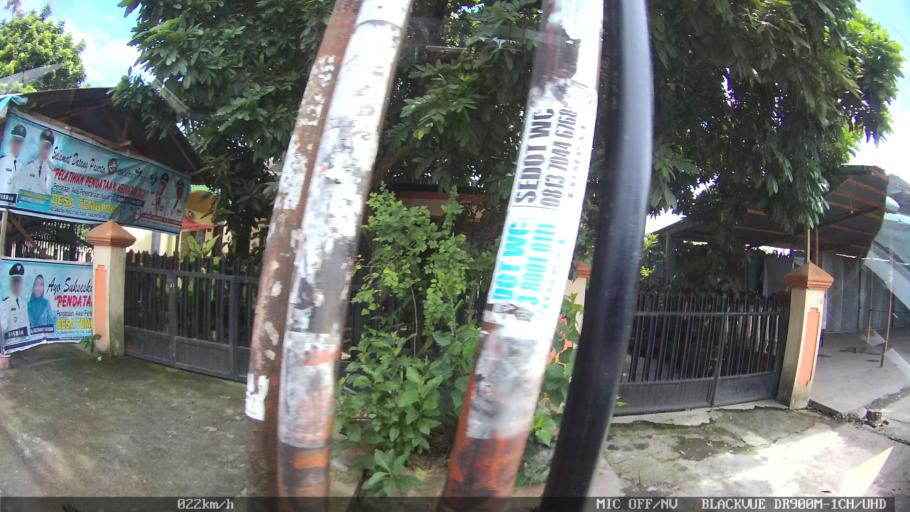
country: ID
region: North Sumatra
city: Medan
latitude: 3.5910
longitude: 98.7517
